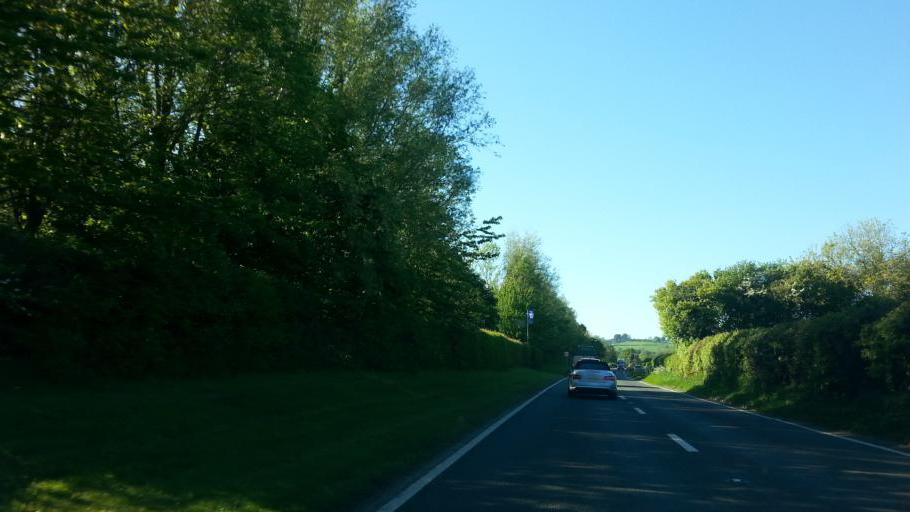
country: GB
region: England
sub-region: Somerset
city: Evercreech
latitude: 51.1530
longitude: -2.5218
